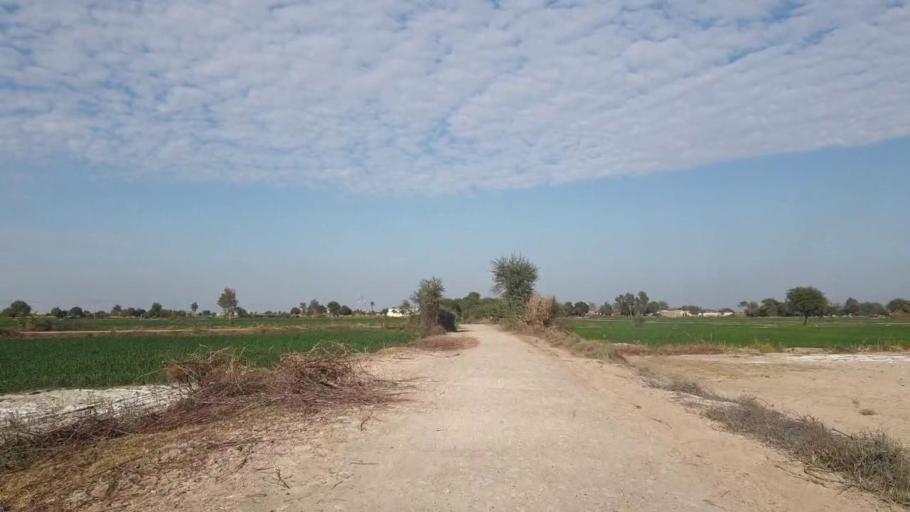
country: PK
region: Sindh
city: Sinjhoro
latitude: 26.0749
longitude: 68.8740
